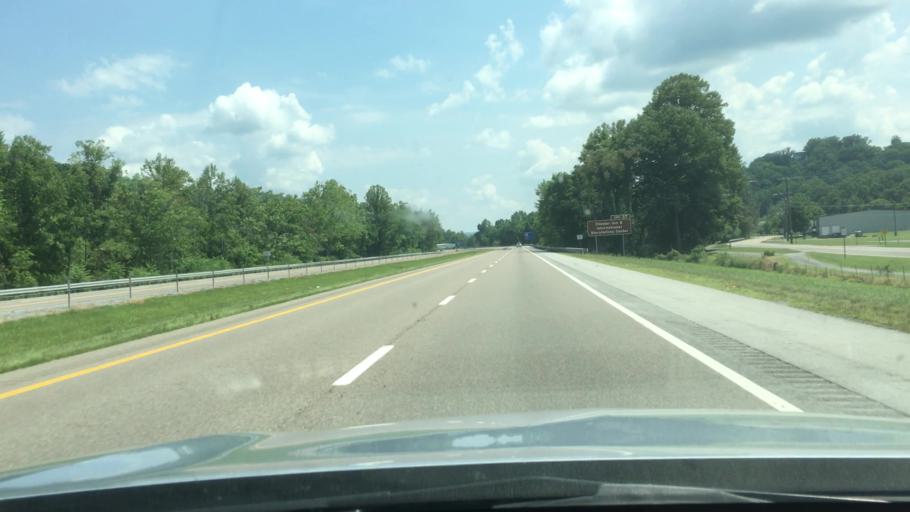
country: US
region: Tennessee
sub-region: Unicoi County
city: Banner Hill
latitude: 36.1322
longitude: -82.4365
